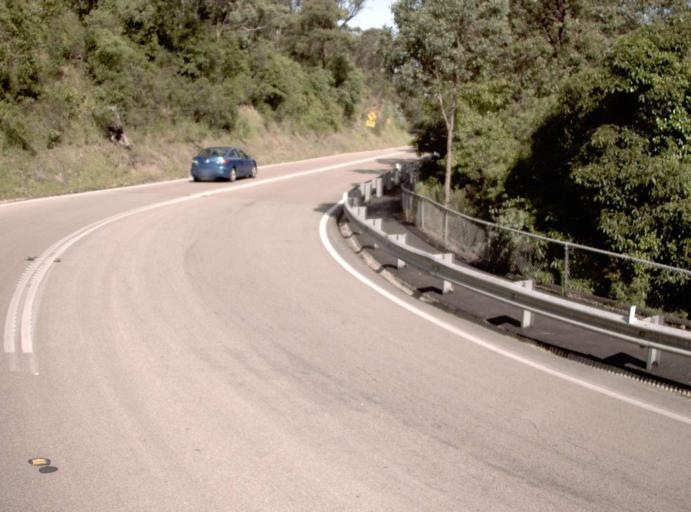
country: AU
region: Victoria
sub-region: East Gippsland
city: Lakes Entrance
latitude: -37.8805
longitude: 147.9664
